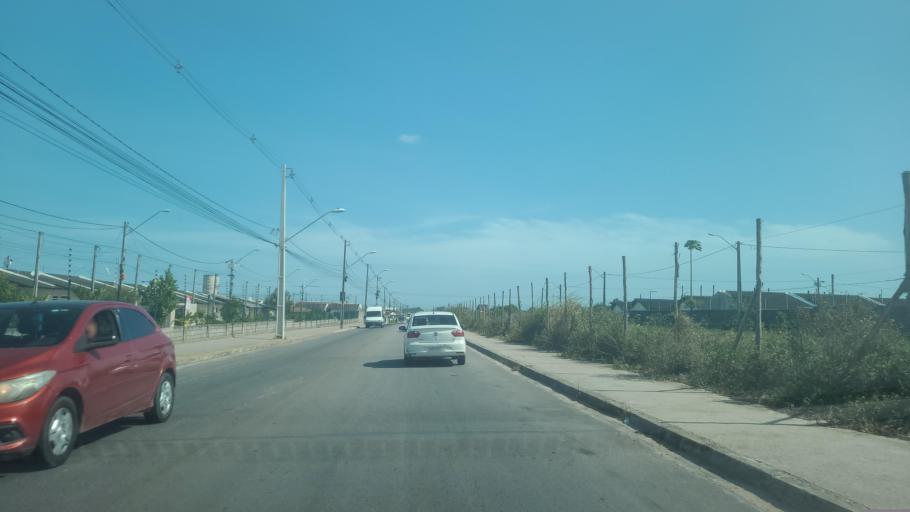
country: BR
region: Alagoas
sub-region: Satuba
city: Satuba
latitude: -9.5286
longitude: -35.7763
